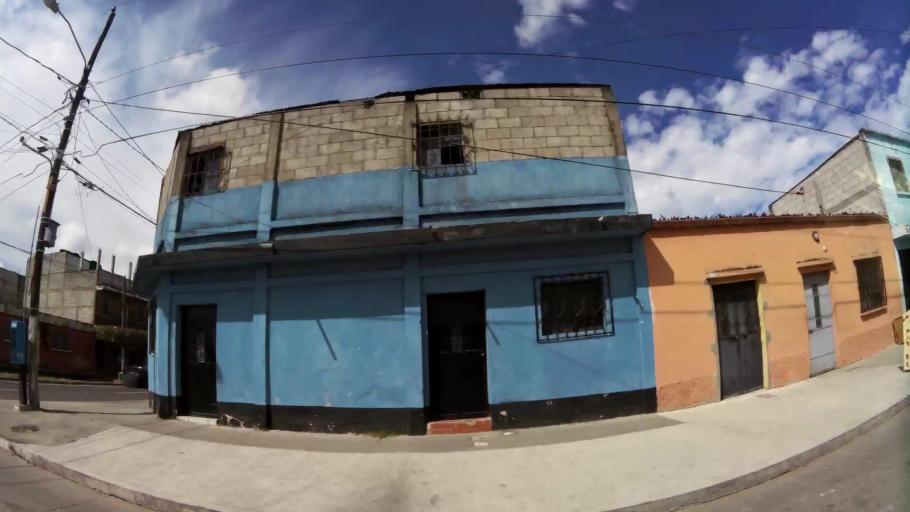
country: GT
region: Guatemala
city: Mixco
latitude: 14.6582
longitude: -90.5756
